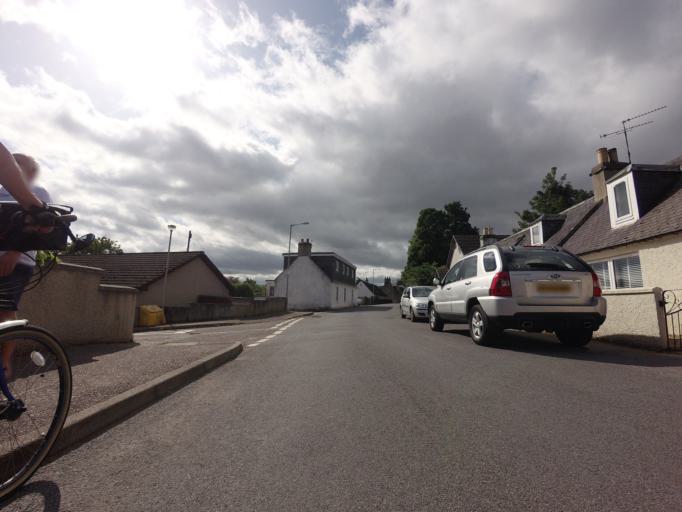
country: GB
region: Scotland
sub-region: Highland
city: Nairn
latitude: 57.5816
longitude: -3.8663
